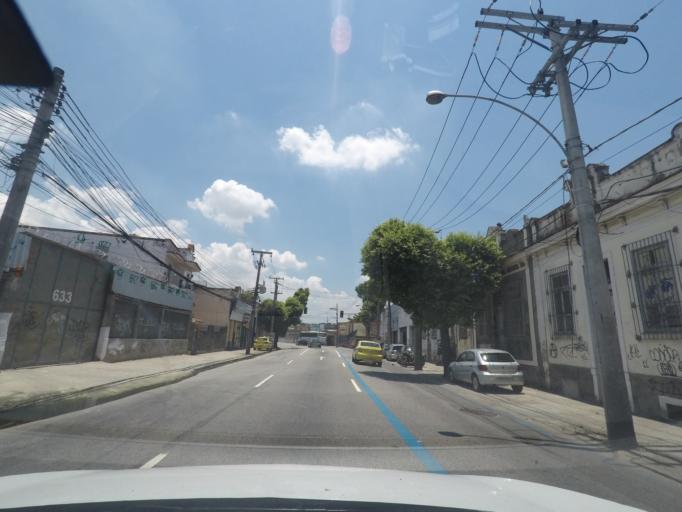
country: BR
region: Rio de Janeiro
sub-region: Rio De Janeiro
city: Rio de Janeiro
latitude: -22.9023
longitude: -43.2607
